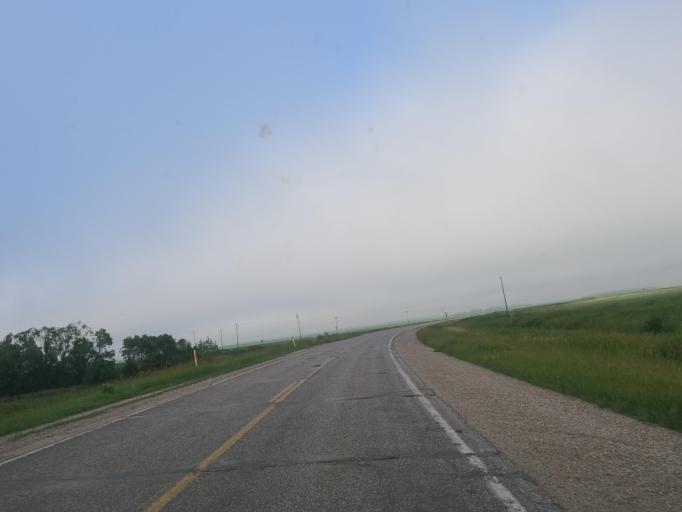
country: CA
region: Manitoba
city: Carman
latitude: 49.6666
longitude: -98.2091
